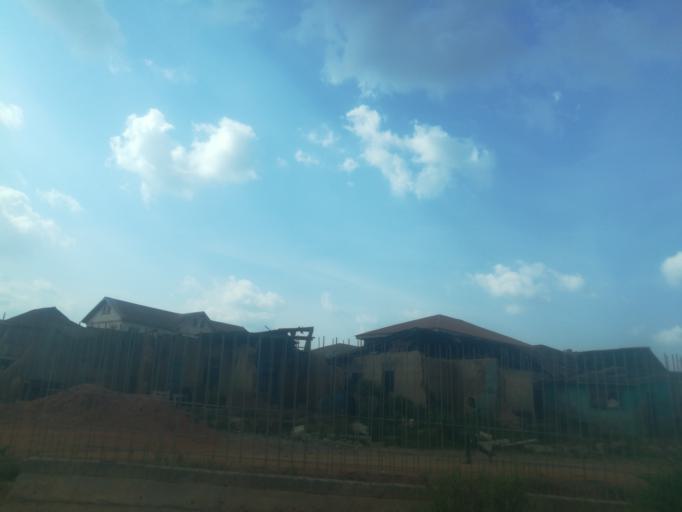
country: NG
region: Ogun
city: Abeokuta
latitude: 7.1791
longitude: 3.3414
